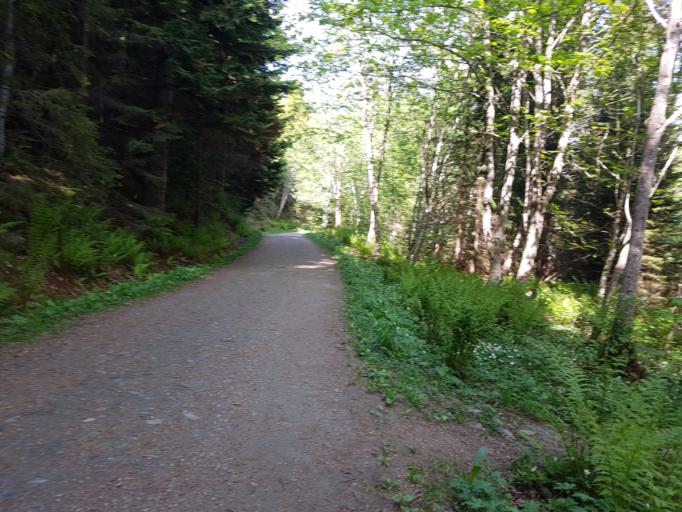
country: NO
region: Sor-Trondelag
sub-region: Trondheim
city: Trondheim
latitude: 63.4297
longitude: 10.3408
